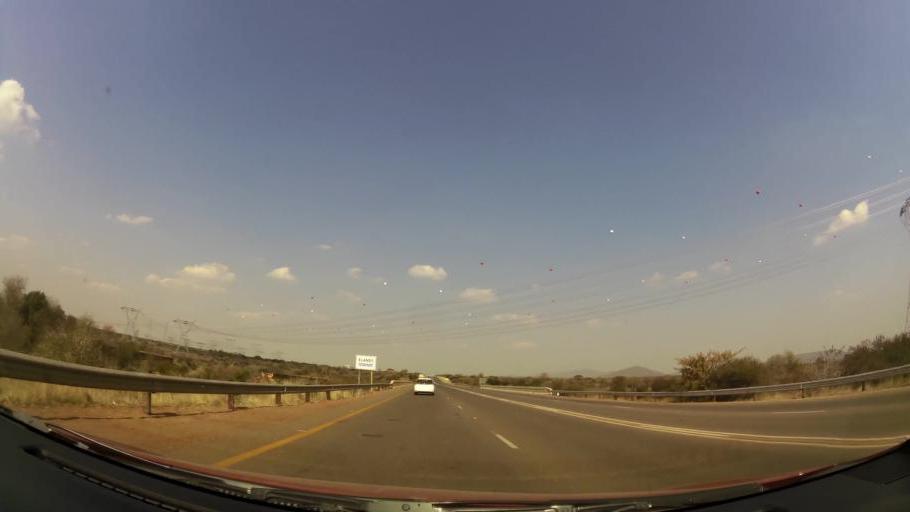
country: ZA
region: North-West
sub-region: Bojanala Platinum District Municipality
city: Mogwase
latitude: -25.3922
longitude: 27.0706
